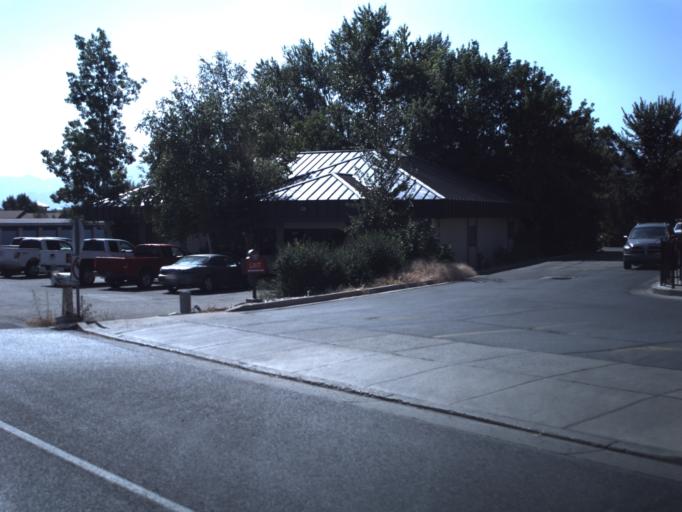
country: US
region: Utah
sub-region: Cache County
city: River Heights
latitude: 41.7150
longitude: -111.8367
